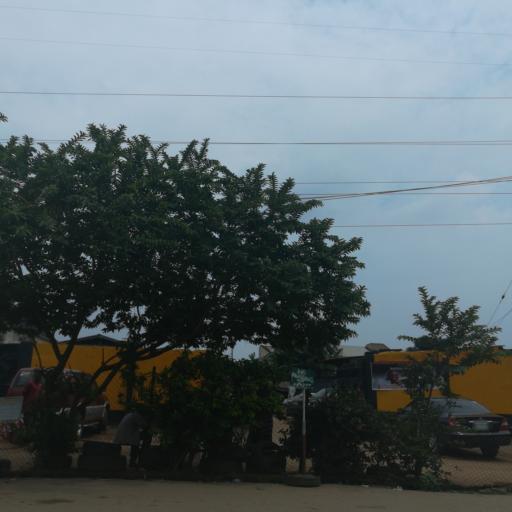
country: NG
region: Lagos
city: Ojota
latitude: 6.5754
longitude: 3.3868
